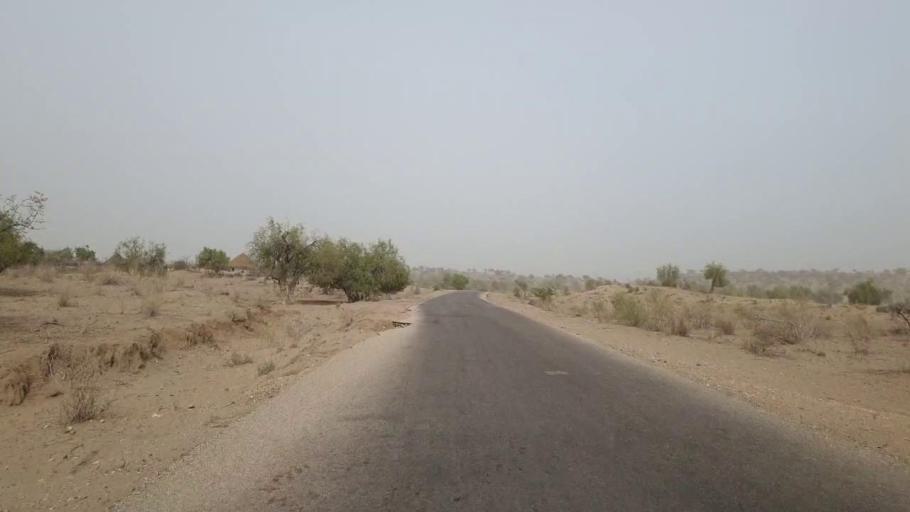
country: PK
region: Sindh
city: Islamkot
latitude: 24.5907
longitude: 70.2873
